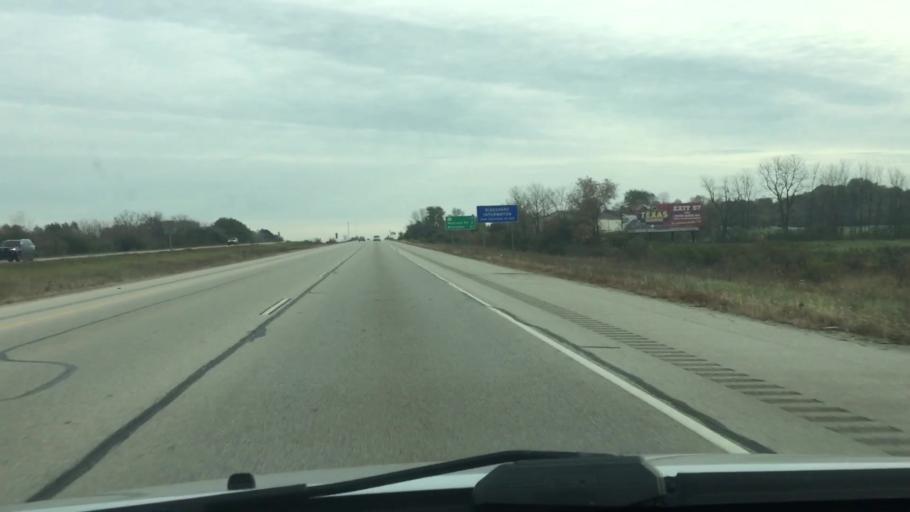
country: US
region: Wisconsin
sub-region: Waukesha County
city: Big Bend
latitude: 42.9159
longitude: -88.2040
